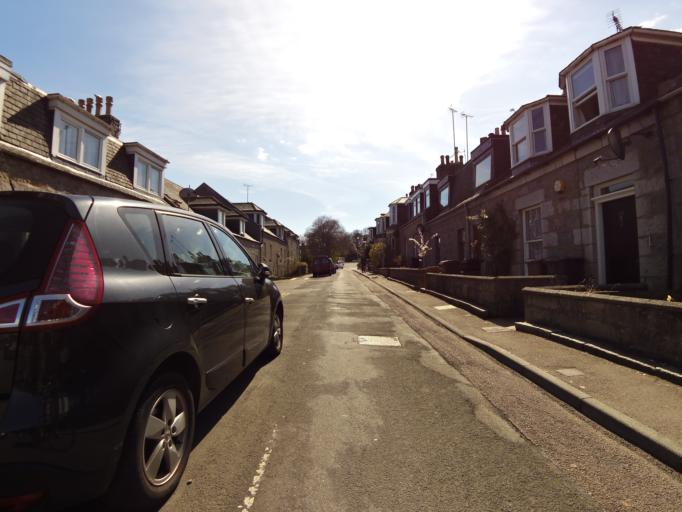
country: GB
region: Scotland
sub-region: Aberdeen City
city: Aberdeen
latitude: 57.1375
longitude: -2.0988
